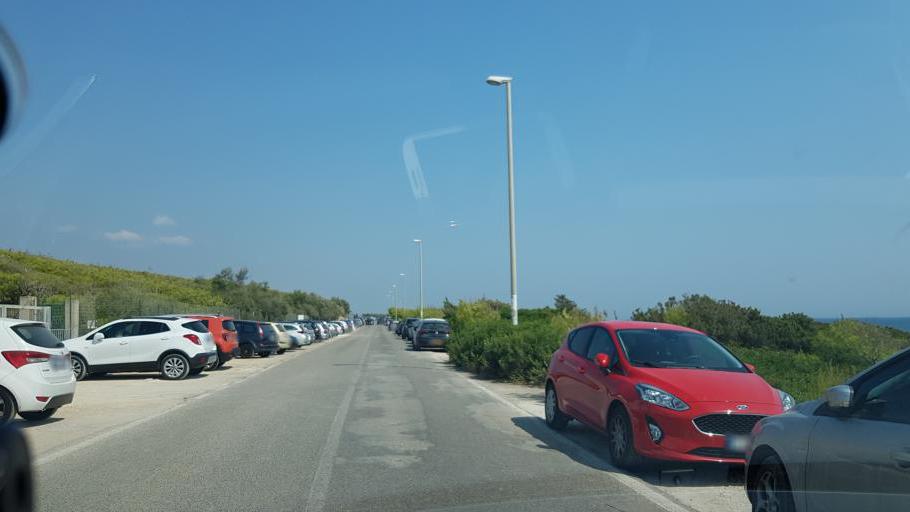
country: IT
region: Apulia
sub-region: Provincia di Taranto
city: Maruggio
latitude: 40.3002
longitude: 17.5755
